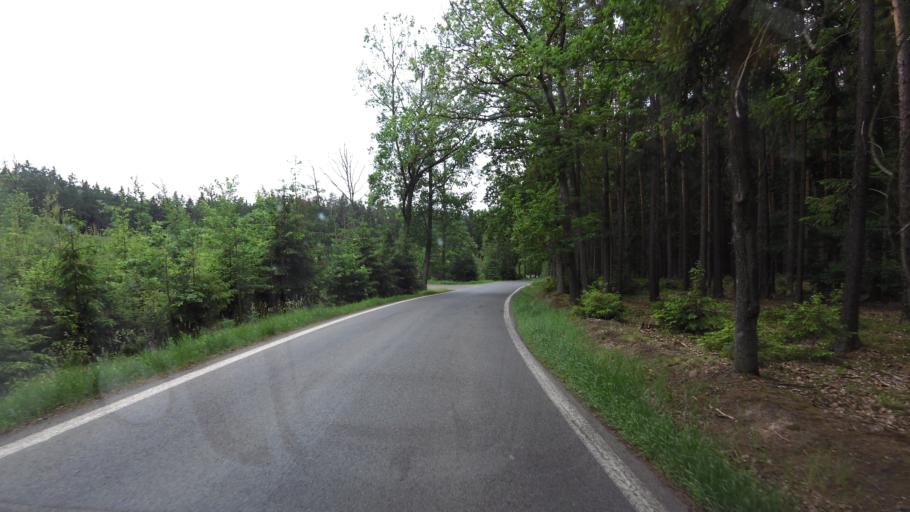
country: CZ
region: Plzensky
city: St'ahlavy
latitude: 49.6916
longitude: 13.5170
